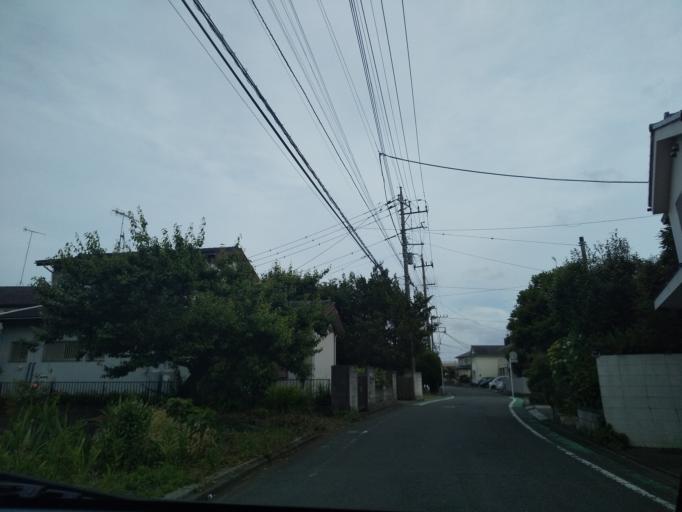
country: JP
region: Kanagawa
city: Zama
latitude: 35.5337
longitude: 139.3773
